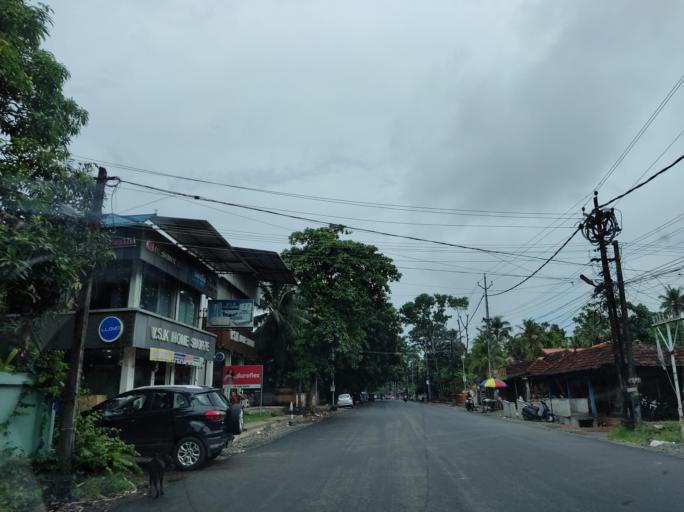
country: IN
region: Kerala
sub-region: Alappuzha
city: Mavelikara
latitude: 9.2507
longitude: 76.5258
